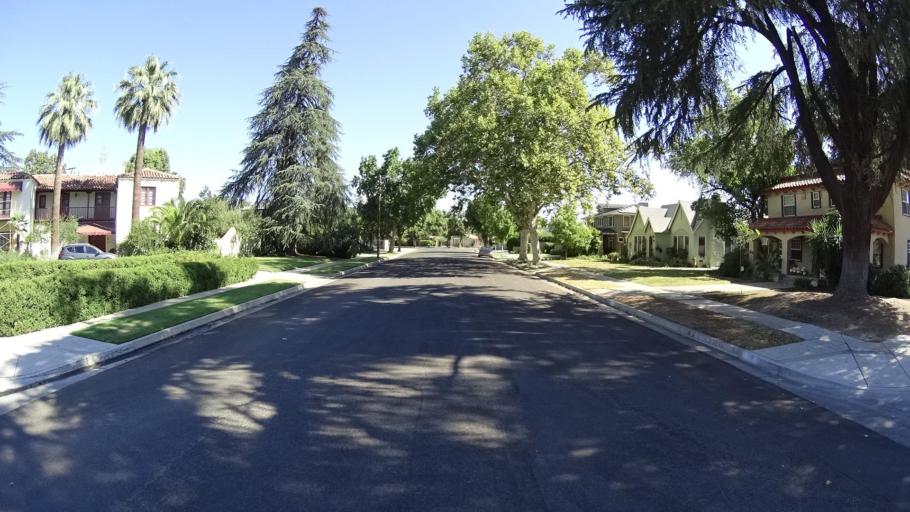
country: US
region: California
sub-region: Fresno County
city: Fresno
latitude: 36.7567
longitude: -119.7963
